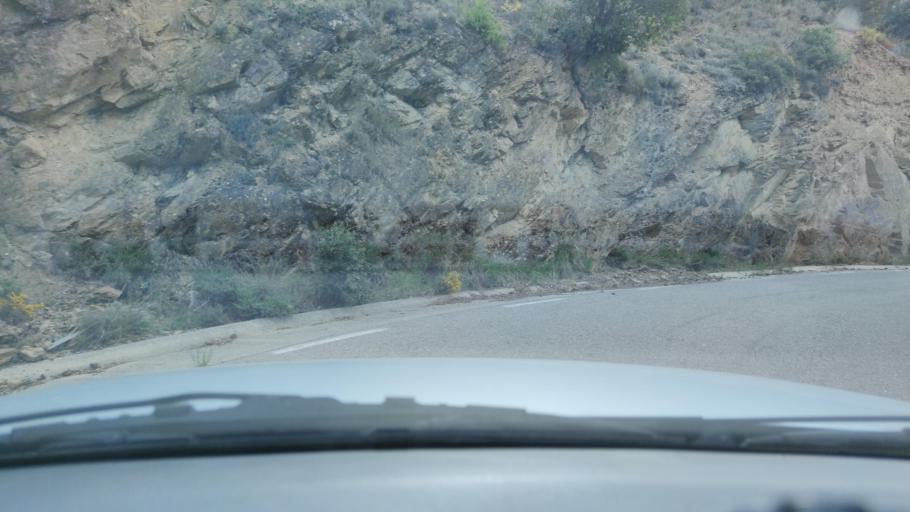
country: ES
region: Catalonia
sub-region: Provincia de Lleida
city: la Seu d'Urgell
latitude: 42.2426
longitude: 1.4276
